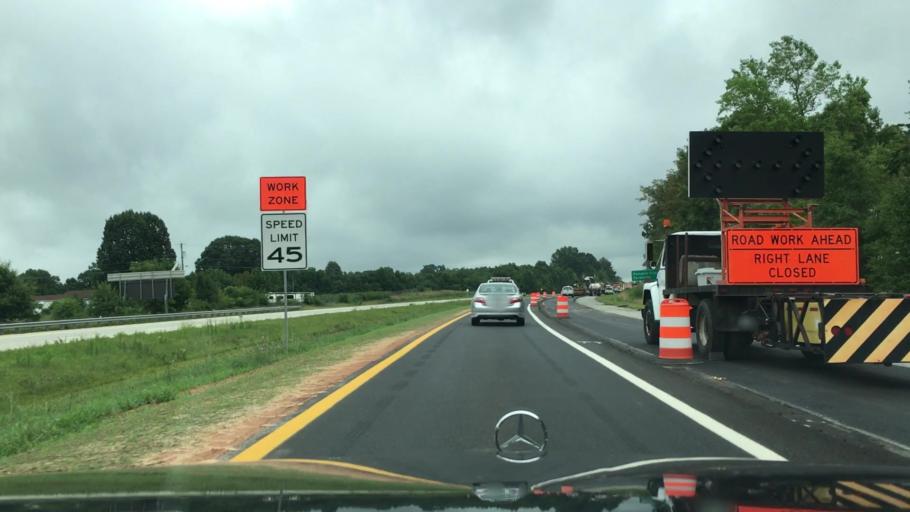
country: US
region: Virginia
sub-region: Appomattox County
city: Appomattox
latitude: 37.3637
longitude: -78.8176
